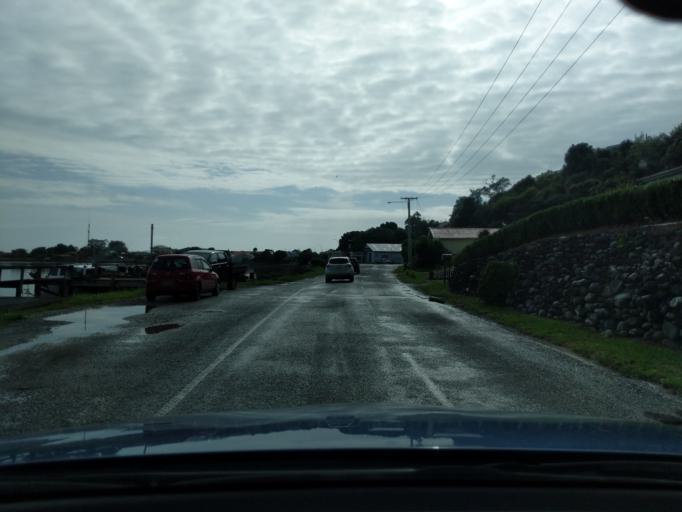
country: NZ
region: Tasman
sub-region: Tasman District
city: Takaka
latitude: -40.6792
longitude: 172.6790
